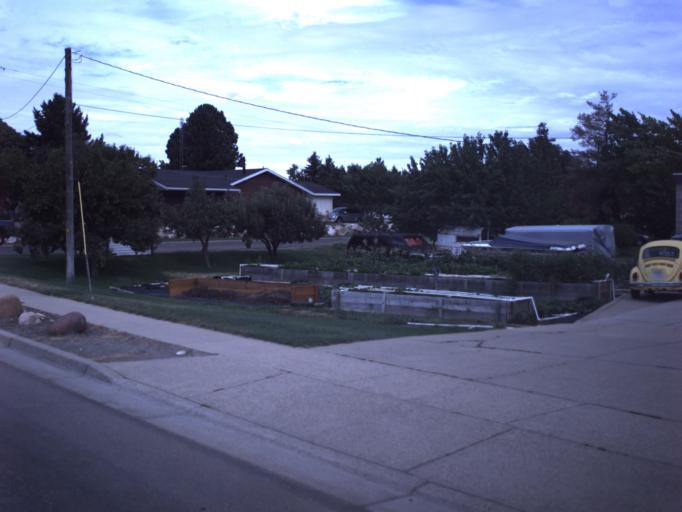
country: US
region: Utah
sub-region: Davis County
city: South Weber
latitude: 41.1327
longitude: -111.9374
